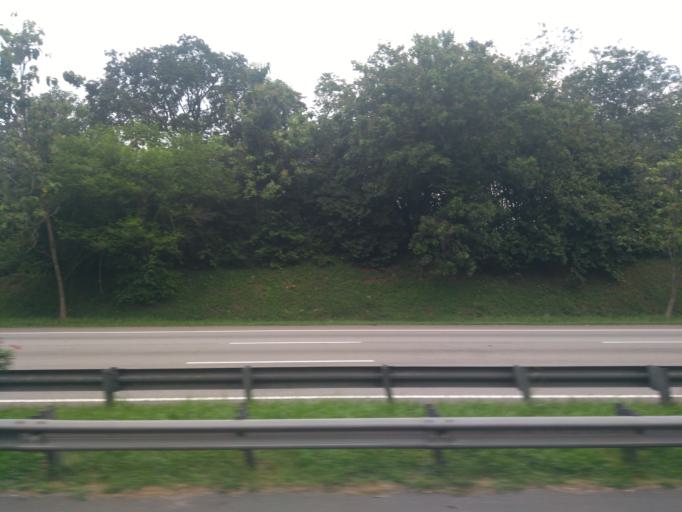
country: MY
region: Melaka
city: Alor Gajah
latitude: 2.3774
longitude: 102.2347
